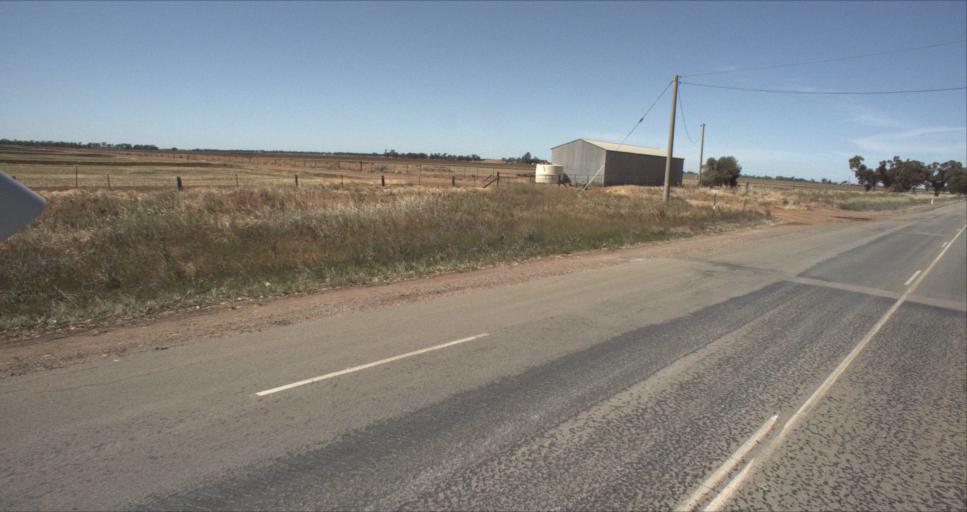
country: AU
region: New South Wales
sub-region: Leeton
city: Leeton
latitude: -34.4996
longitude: 146.2872
